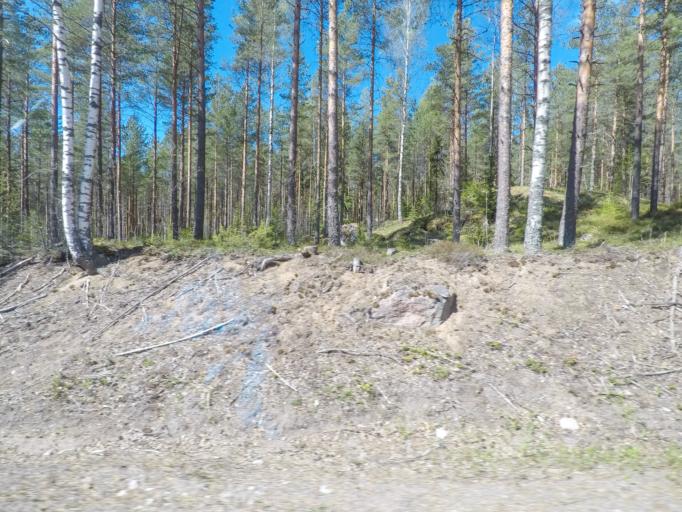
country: FI
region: Uusimaa
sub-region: Helsinki
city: Kaerkoelae
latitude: 60.4883
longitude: 23.8600
